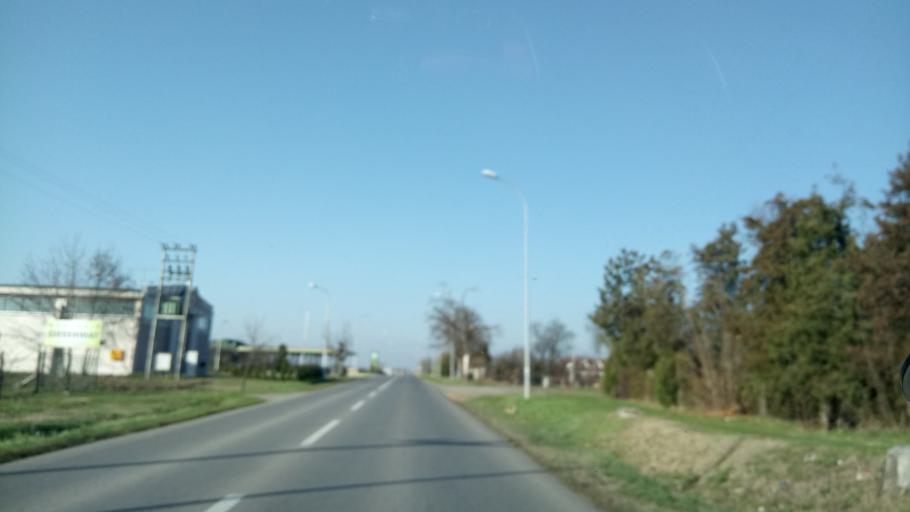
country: RS
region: Autonomna Pokrajina Vojvodina
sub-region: Sremski Okrug
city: Ingija
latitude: 45.0628
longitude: 20.0604
